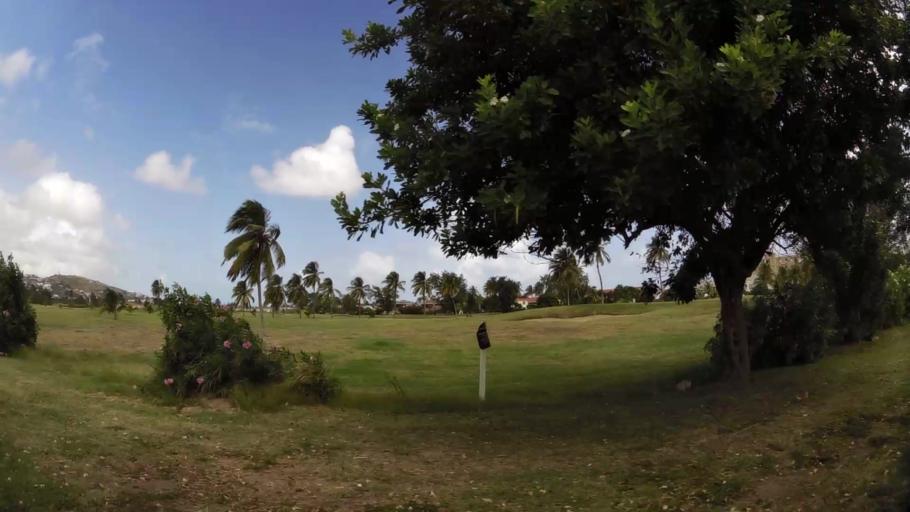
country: KN
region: Saint George Basseterre
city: Basseterre
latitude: 17.2841
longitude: -62.6860
